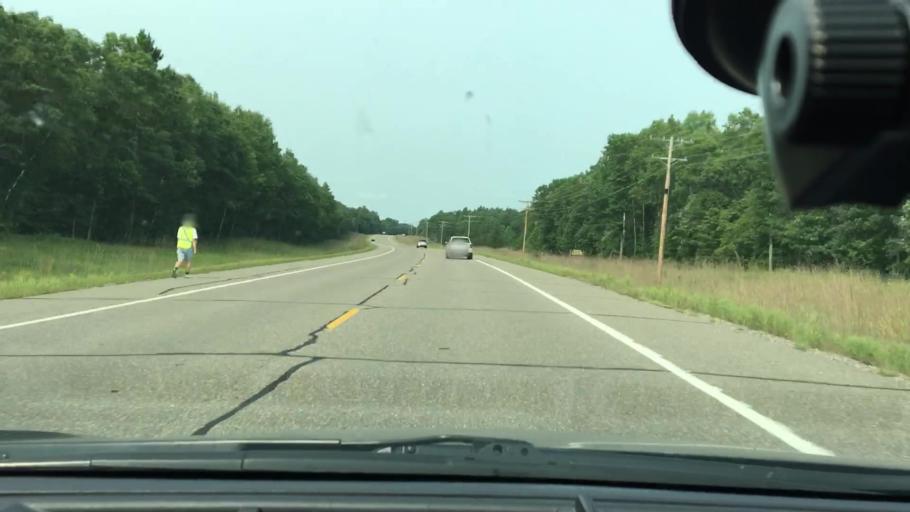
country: US
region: Minnesota
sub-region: Crow Wing County
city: Cross Lake
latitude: 46.6031
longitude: -94.1306
